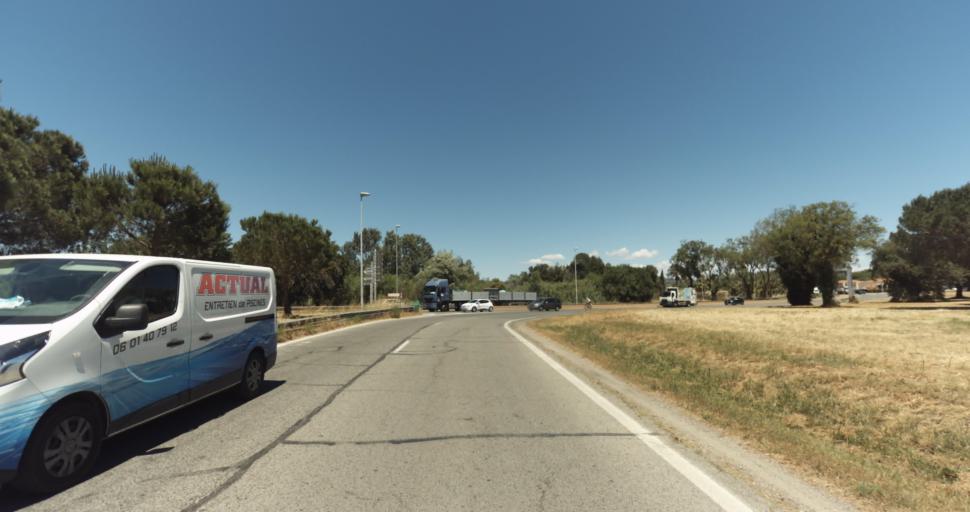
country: FR
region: Provence-Alpes-Cote d'Azur
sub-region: Departement du Var
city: Gassin
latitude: 43.2624
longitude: 6.5748
